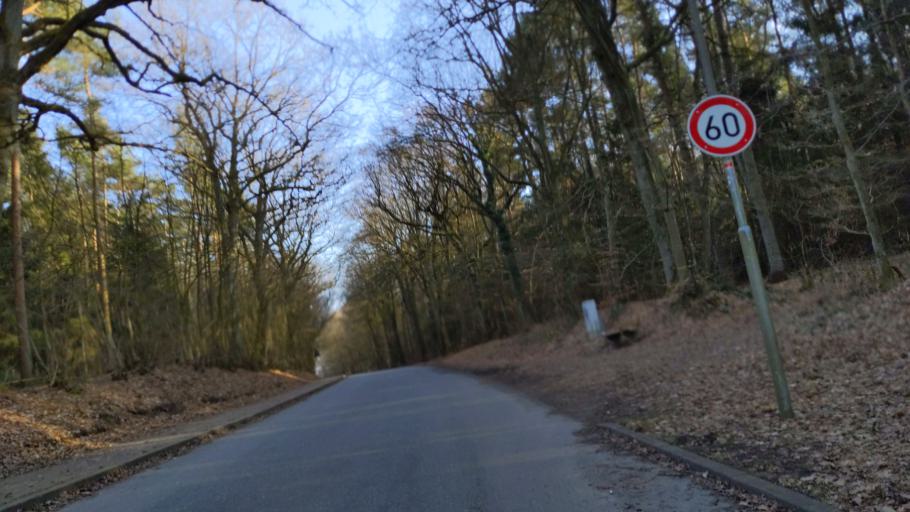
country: DE
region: Schleswig-Holstein
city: Ratekau
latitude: 53.9695
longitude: 10.7049
